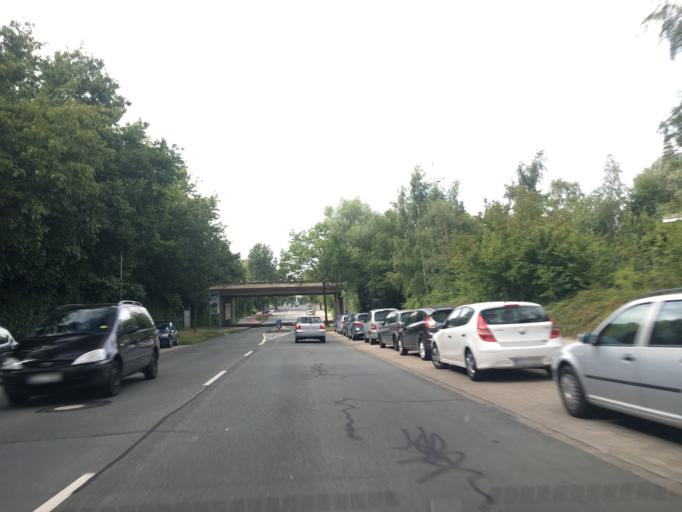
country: DE
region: North Rhine-Westphalia
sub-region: Regierungsbezirk Munster
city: Muenster
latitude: 51.9256
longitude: 7.6499
